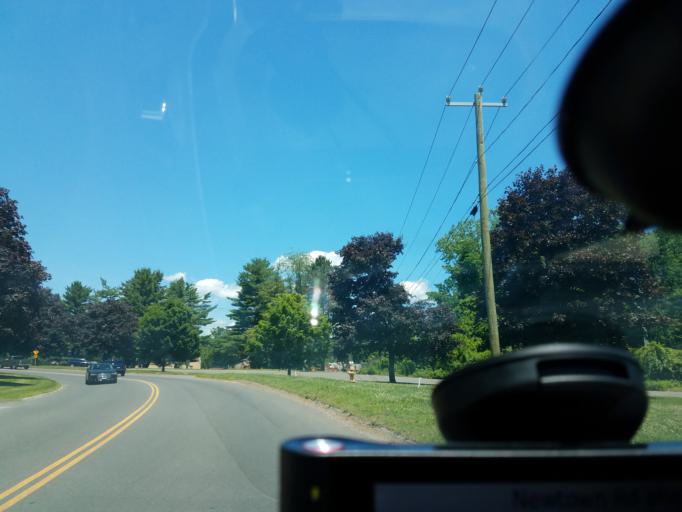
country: US
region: Connecticut
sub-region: Fairfield County
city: Bethel
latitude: 41.4031
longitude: -73.4144
